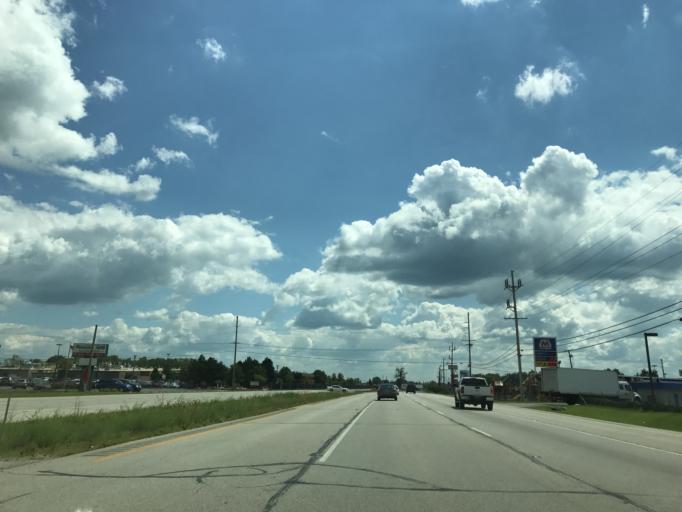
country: US
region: Indiana
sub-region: Kosciusko County
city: Winona Lake
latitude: 41.2332
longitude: -85.8045
